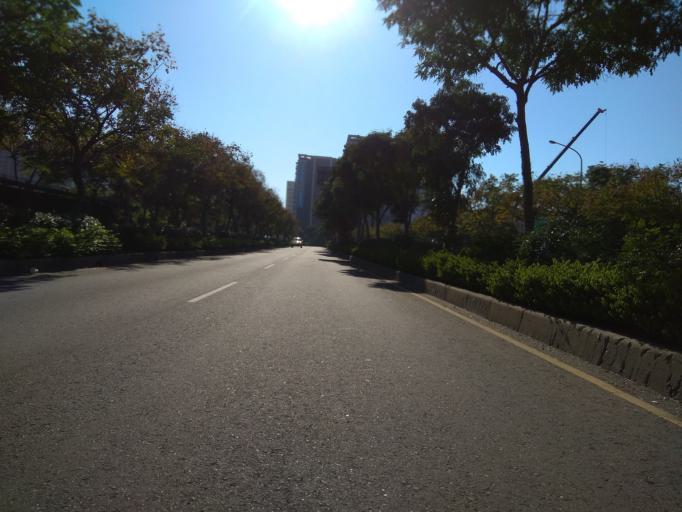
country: TW
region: Taiwan
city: Taoyuan City
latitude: 25.0173
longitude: 121.2233
